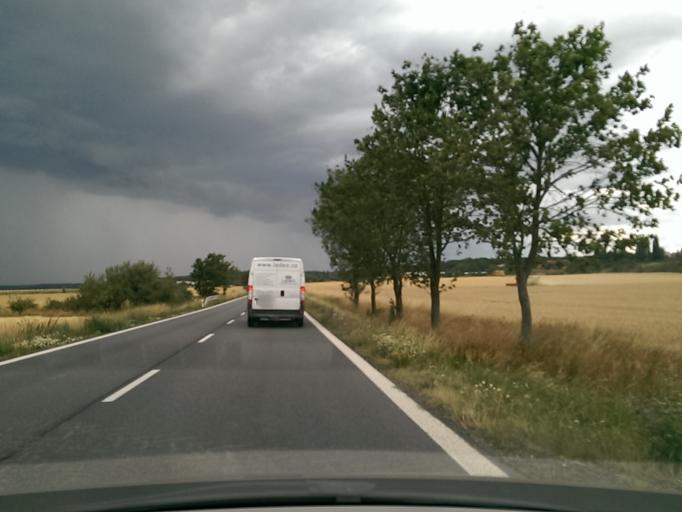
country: CZ
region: Central Bohemia
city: Loucen
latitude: 50.2490
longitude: 15.0013
